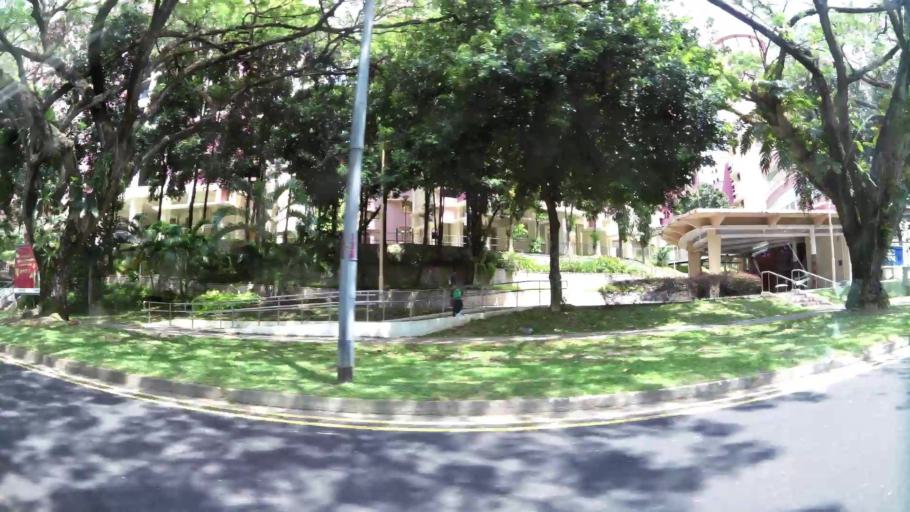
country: MY
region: Johor
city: Kampung Pasir Gudang Baru
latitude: 1.4357
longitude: 103.8344
